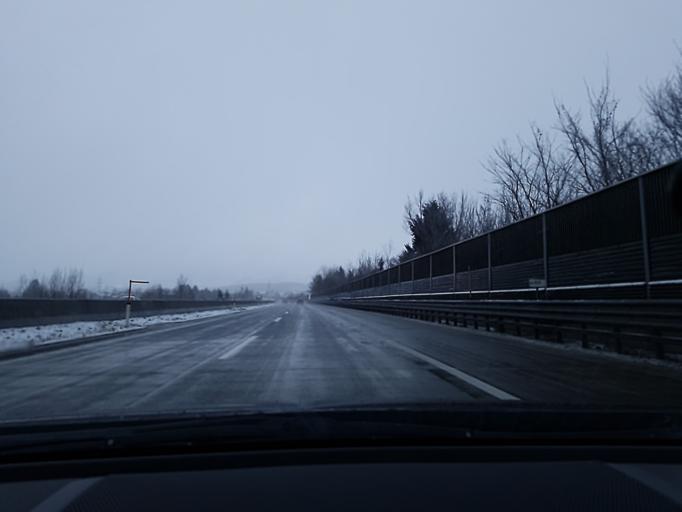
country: AT
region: Salzburg
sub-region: Politischer Bezirk Hallein
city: Kuchl
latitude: 47.6369
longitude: 13.1343
